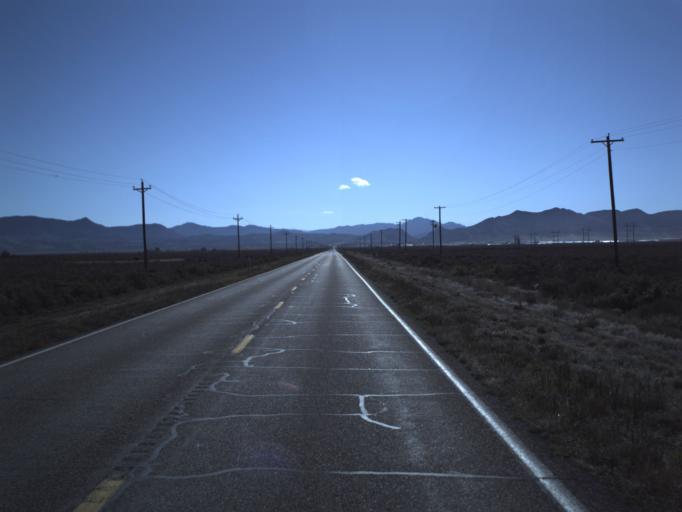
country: US
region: Utah
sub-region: Washington County
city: Enterprise
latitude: 37.7023
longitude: -113.6363
